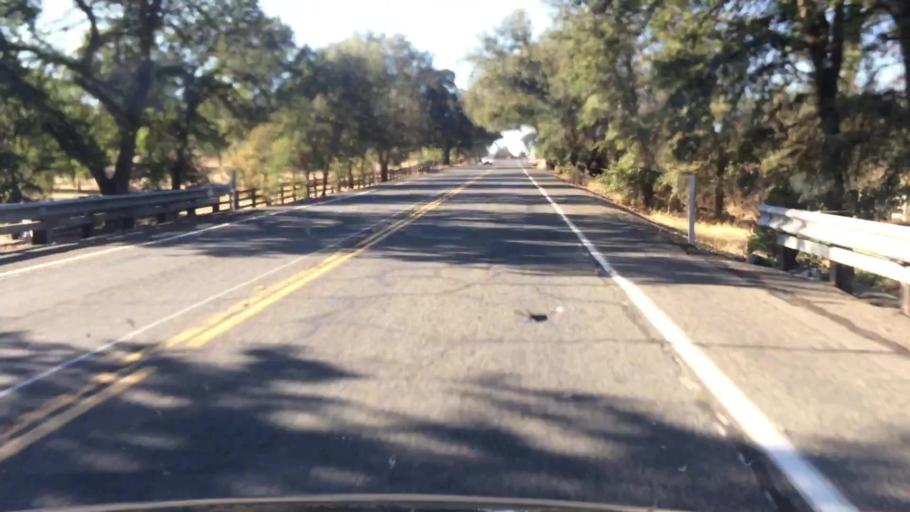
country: US
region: California
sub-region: Sacramento County
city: Wilton
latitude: 38.4282
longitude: -121.2004
